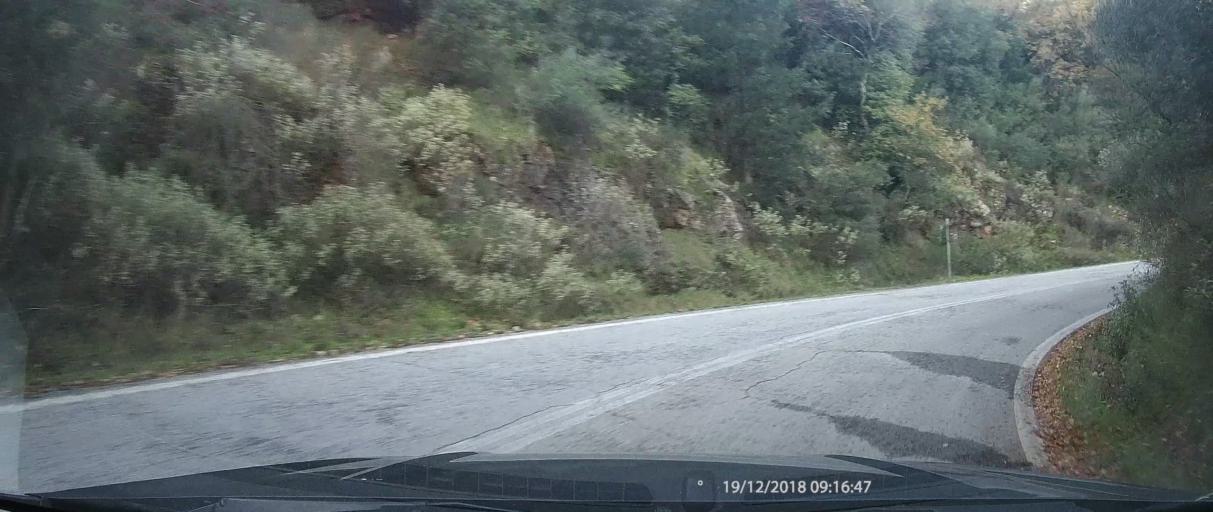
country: GR
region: Peloponnese
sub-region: Nomos Lakonias
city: Magoula
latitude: 37.0915
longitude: 22.3664
